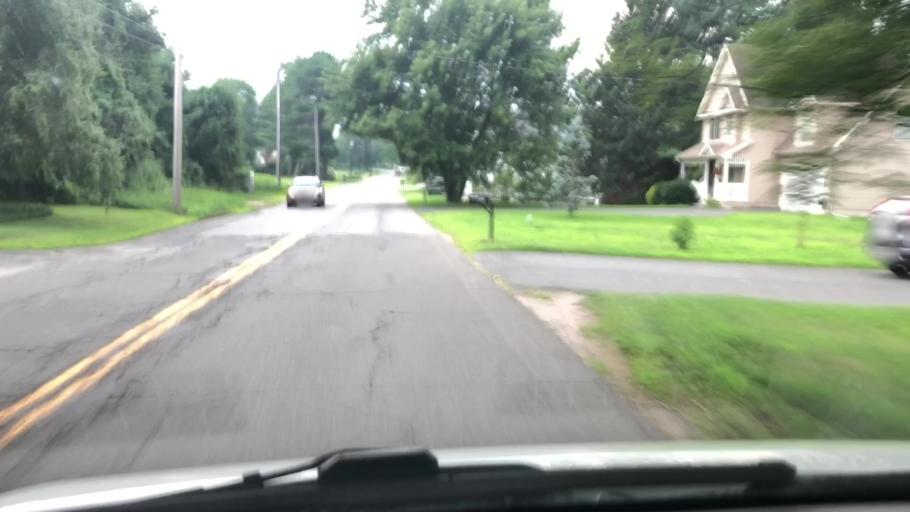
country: US
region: Massachusetts
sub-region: Hampshire County
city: Easthampton
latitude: 42.2598
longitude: -72.6504
